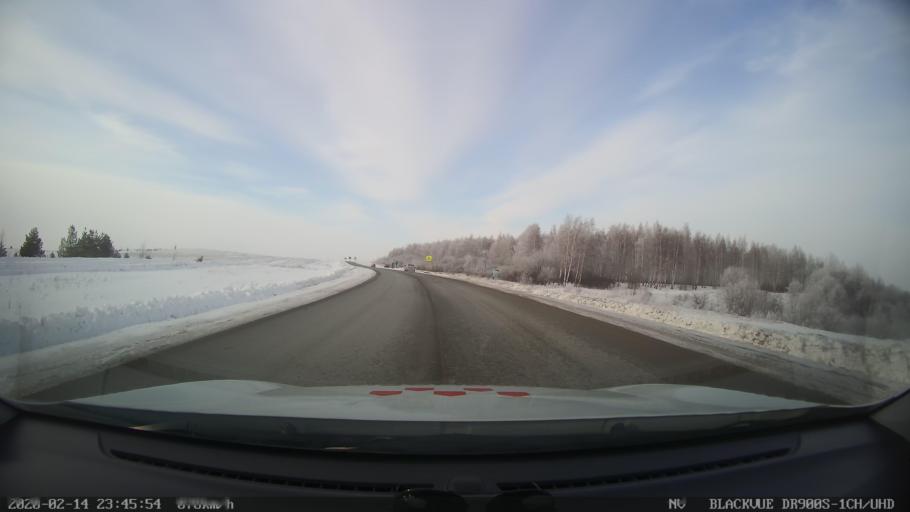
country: RU
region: Tatarstan
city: Kuybyshevskiy Zaton
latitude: 55.2262
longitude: 49.2322
